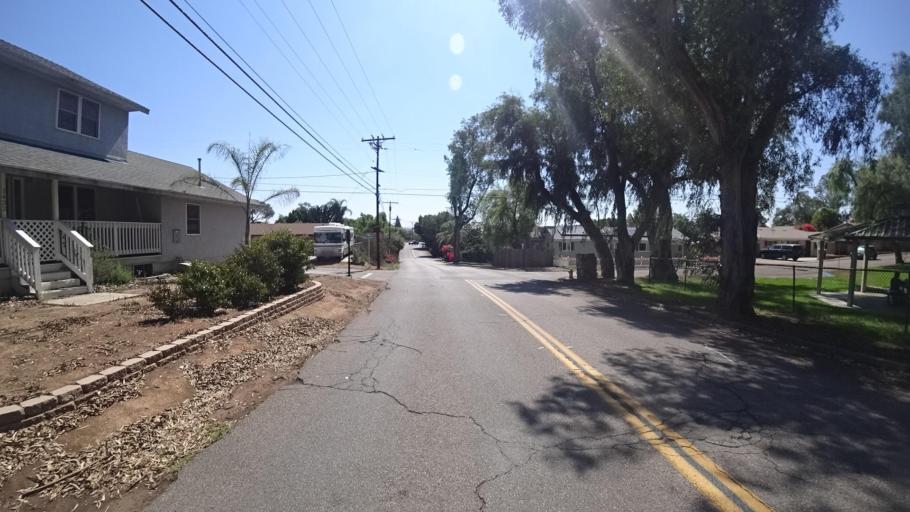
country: US
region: California
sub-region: San Diego County
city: Crest
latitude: 32.8095
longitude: -116.8636
